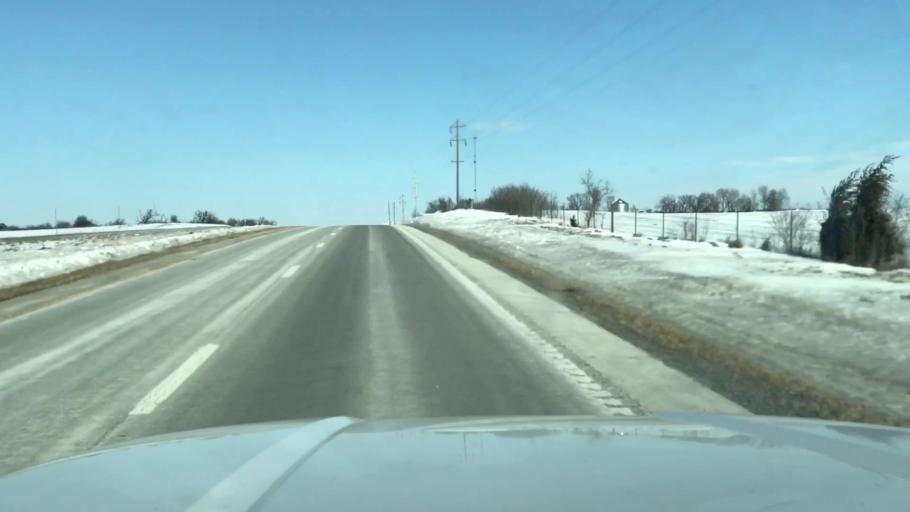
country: US
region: Missouri
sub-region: Nodaway County
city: Maryville
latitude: 40.1741
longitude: -94.8687
